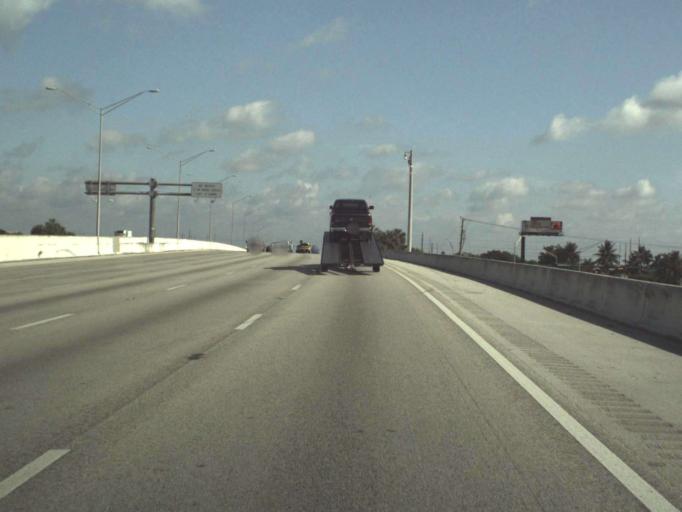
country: US
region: Florida
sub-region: Palm Beach County
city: Mangonia Park
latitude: 26.7571
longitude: -80.0902
